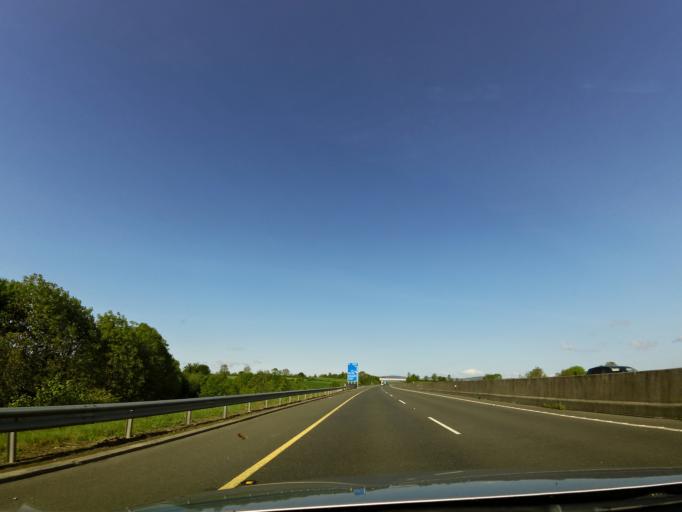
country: IE
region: Munster
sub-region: North Tipperary
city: Nenagh
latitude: 52.8443
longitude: -8.2193
